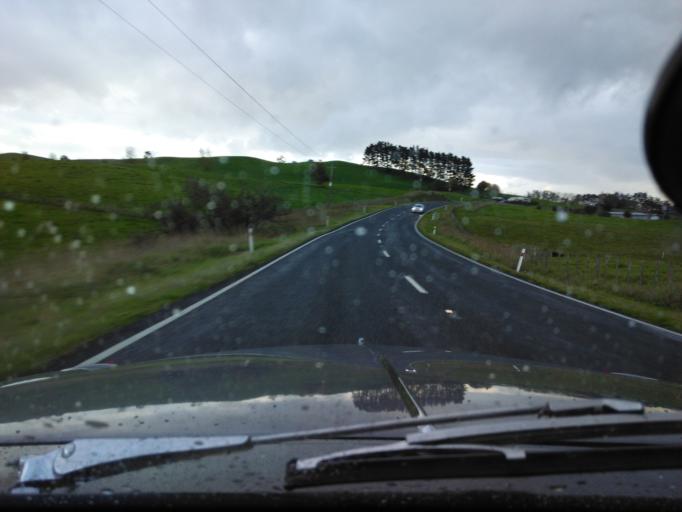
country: NZ
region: Waikato
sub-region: Hauraki District
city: Ngatea
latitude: -37.5103
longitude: 175.4645
